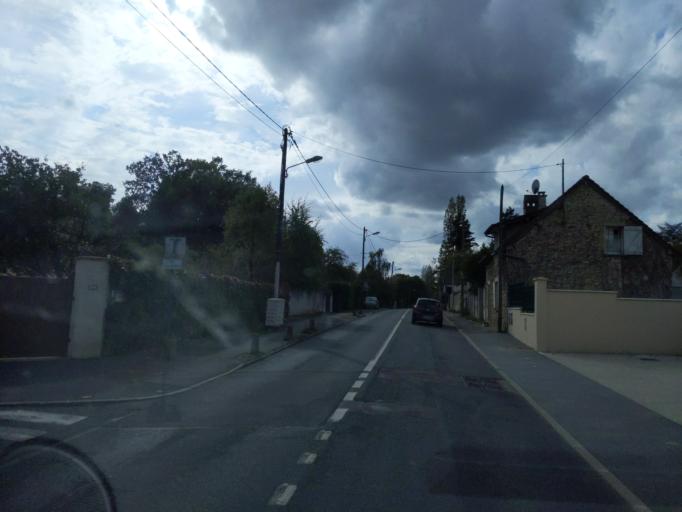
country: FR
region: Ile-de-France
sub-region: Departement des Yvelines
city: Rambouillet
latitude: 48.6479
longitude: 1.8650
